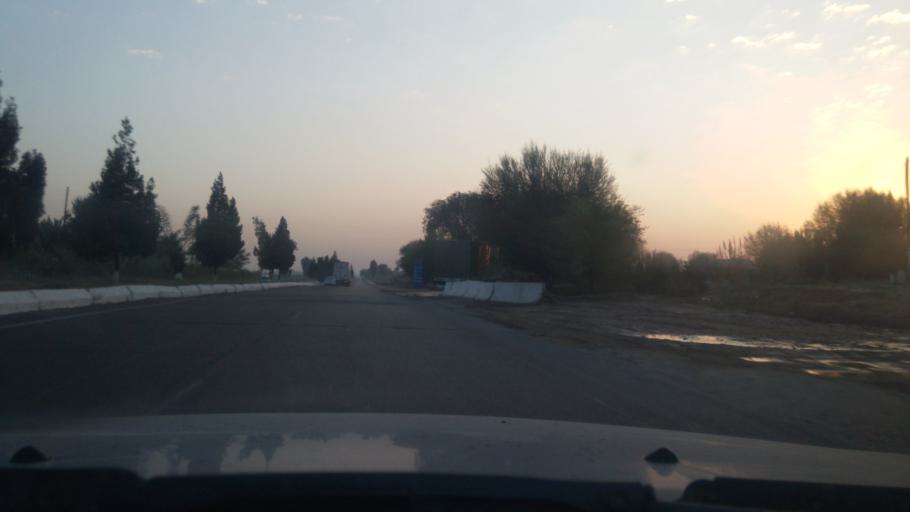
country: UZ
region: Toshkent
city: Zafar
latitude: 41.0406
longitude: 68.8814
